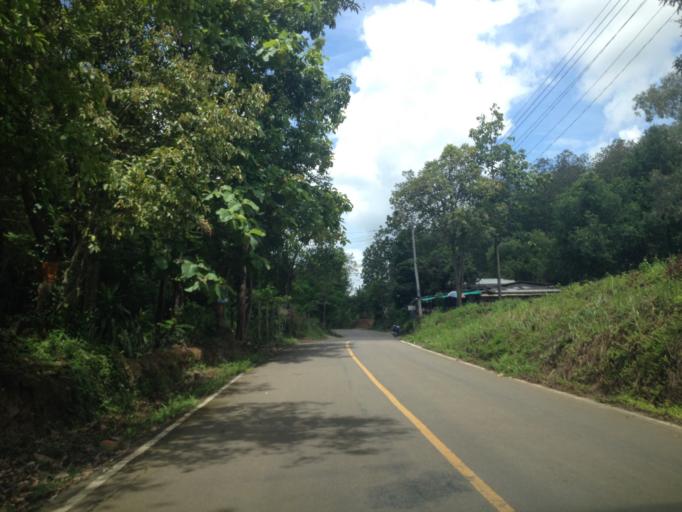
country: TH
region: Chiang Mai
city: Hang Dong
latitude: 18.7149
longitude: 98.8940
